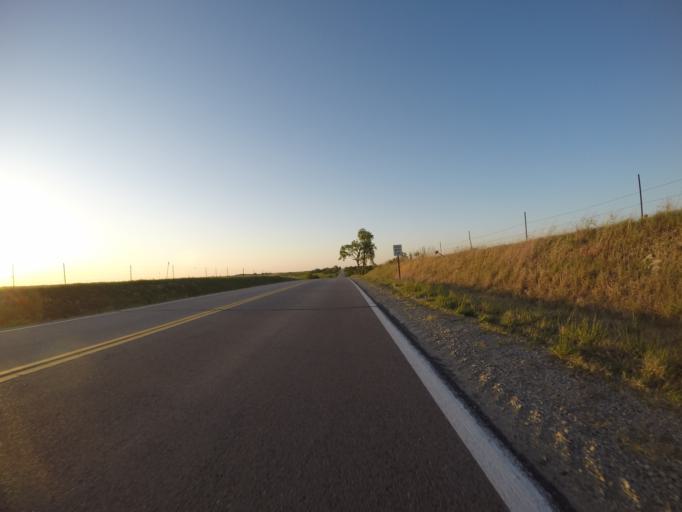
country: US
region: Kansas
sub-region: Riley County
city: Fort Riley North
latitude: 39.2701
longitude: -96.7751
